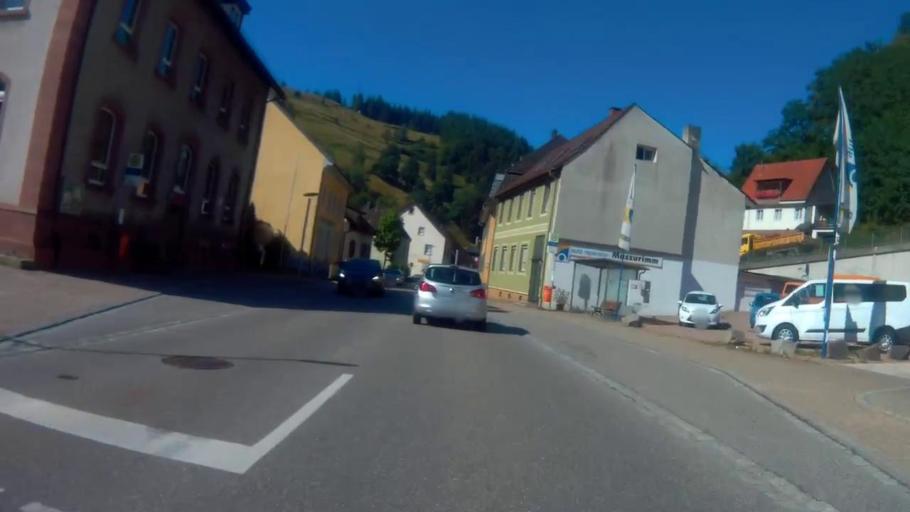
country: DE
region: Baden-Wuerttemberg
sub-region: Freiburg Region
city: Zell im Wiesental
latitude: 47.7146
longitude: 7.8723
